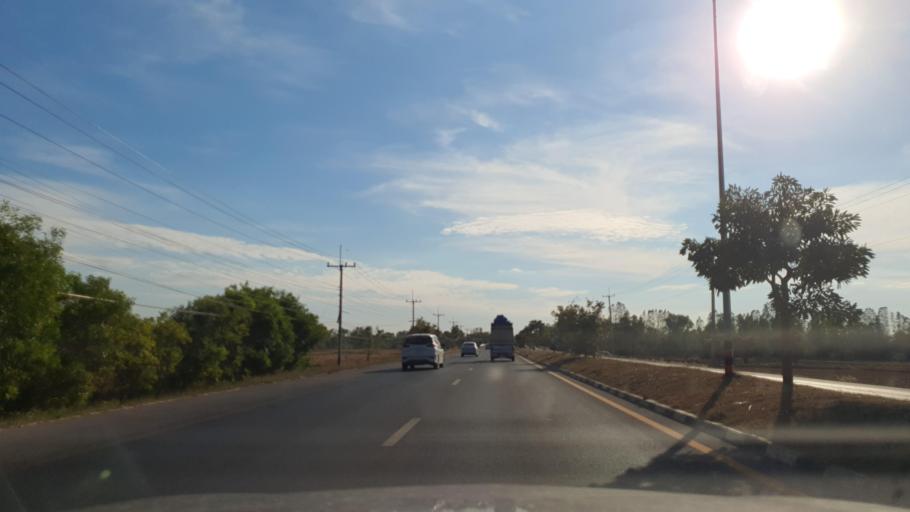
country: TH
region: Kalasin
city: Yang Talat
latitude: 16.3652
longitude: 103.3413
